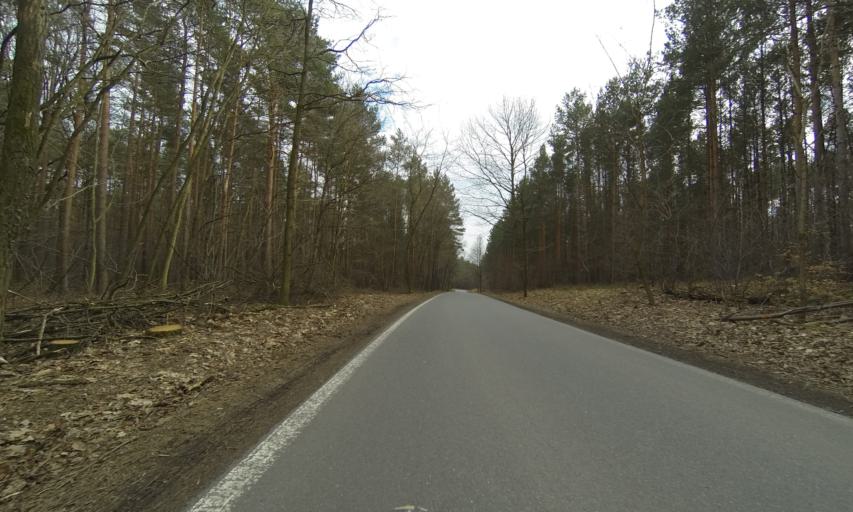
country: DE
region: Saxony
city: Radebeul
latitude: 51.1100
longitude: 13.7146
